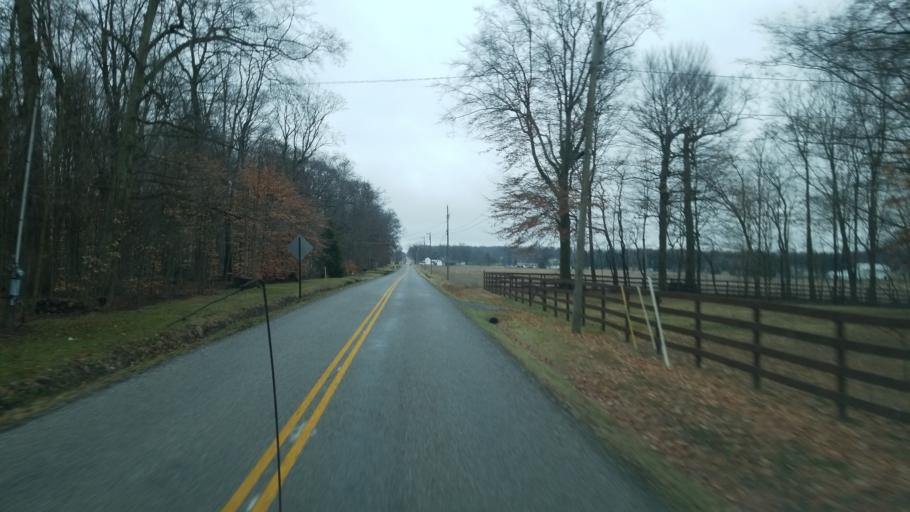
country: US
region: Ohio
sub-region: Wayne County
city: Orrville
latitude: 40.8799
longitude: -81.7837
